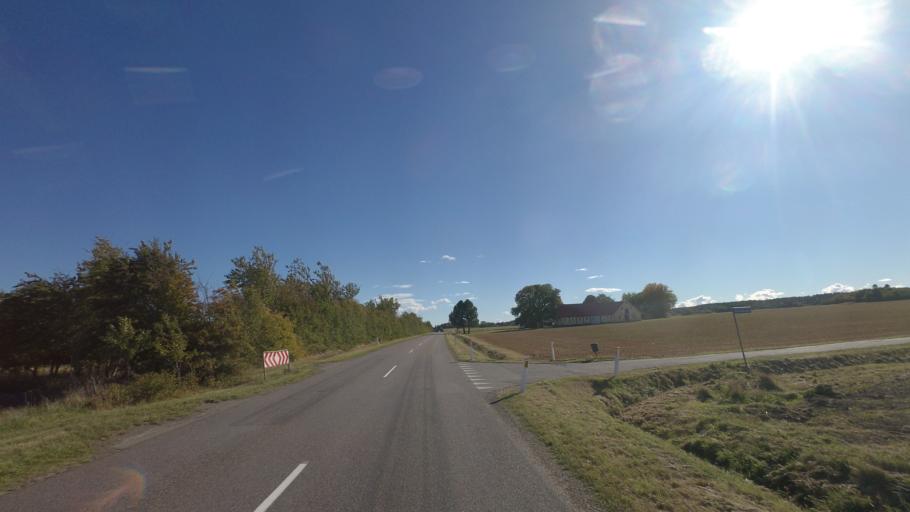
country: DK
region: Capital Region
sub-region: Bornholm Kommune
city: Nexo
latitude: 55.1127
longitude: 15.1096
